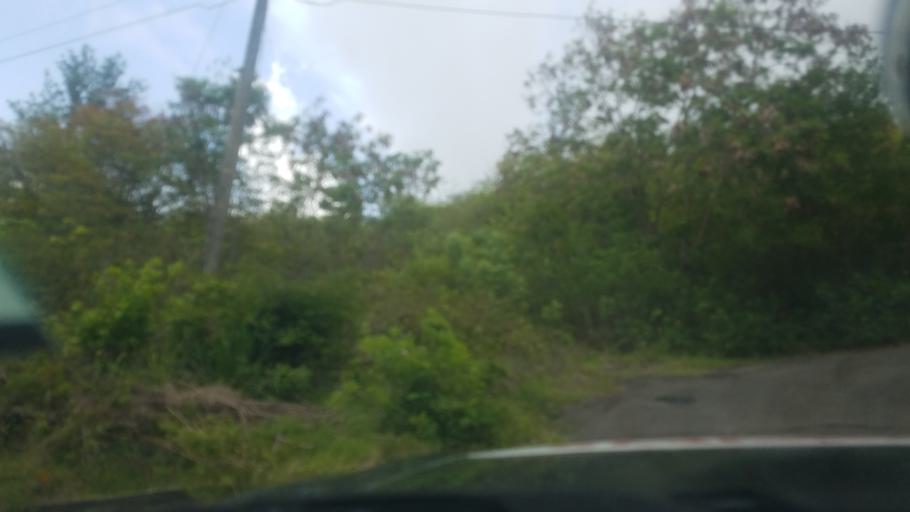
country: LC
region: Laborie Quarter
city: Laborie
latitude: 13.7438
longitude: -60.9679
